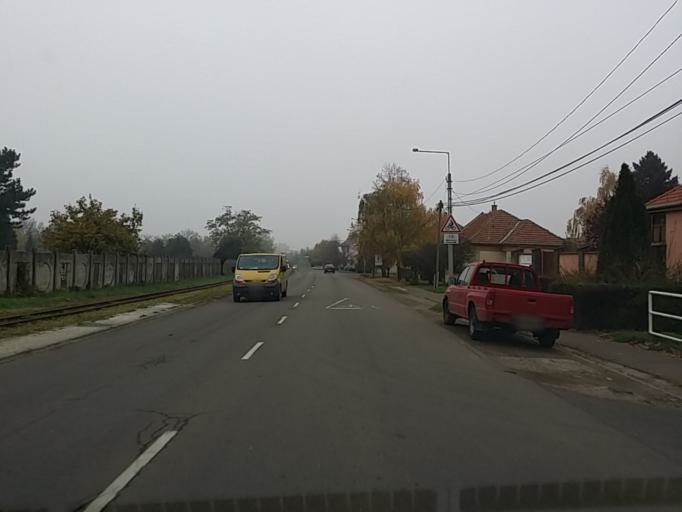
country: HU
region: Heves
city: Gyongyos
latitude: 47.7938
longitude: 19.9396
